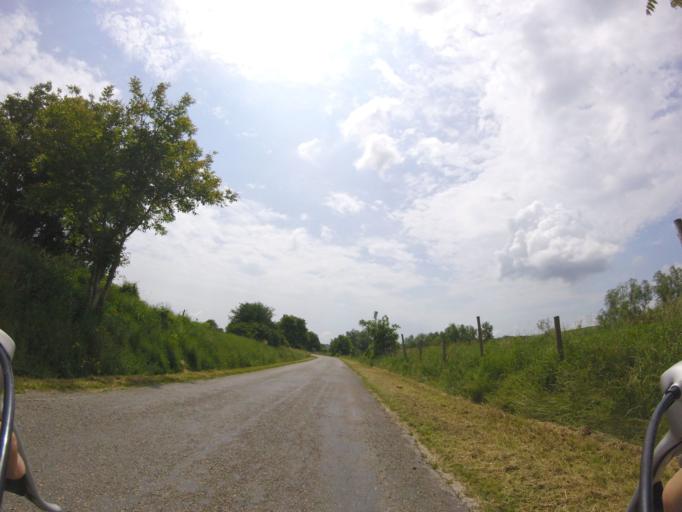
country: HU
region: Baranya
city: Kozarmisleny
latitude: 46.0439
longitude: 18.3832
